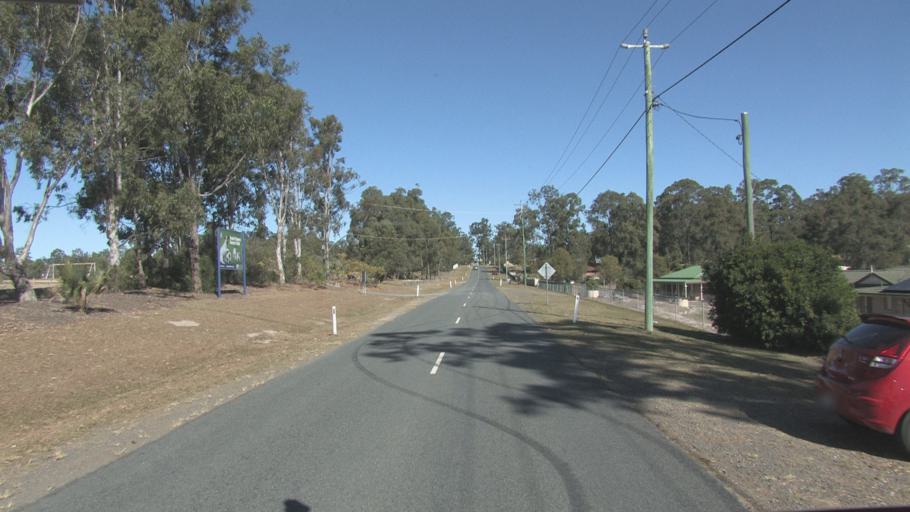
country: AU
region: Queensland
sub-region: Logan
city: North Maclean
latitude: -27.7274
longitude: 152.9620
